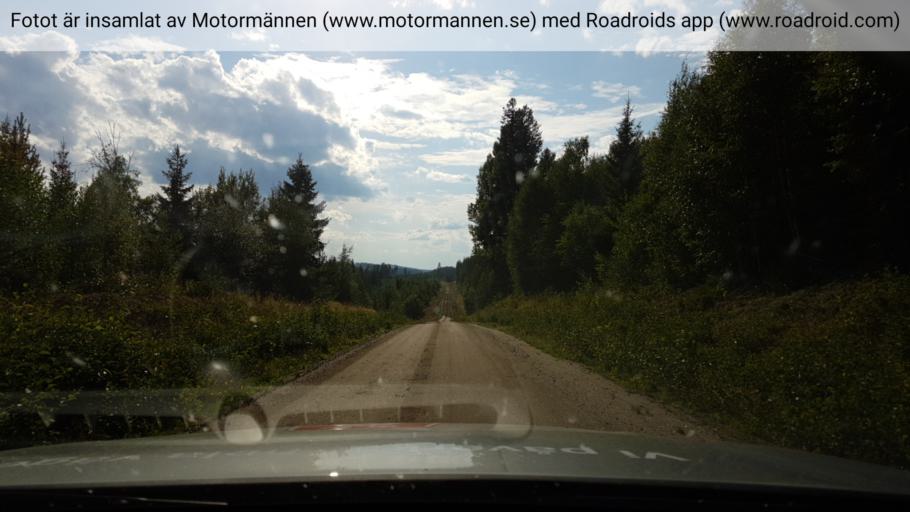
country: SE
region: Jaemtland
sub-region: Stroemsunds Kommun
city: Stroemsund
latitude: 63.7206
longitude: 16.0669
